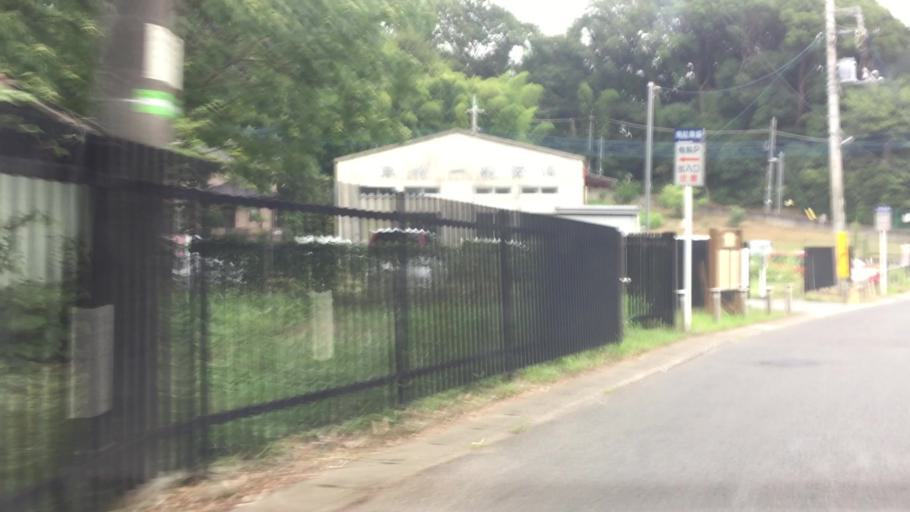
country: JP
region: Chiba
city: Matsudo
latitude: 35.7993
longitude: 139.9360
